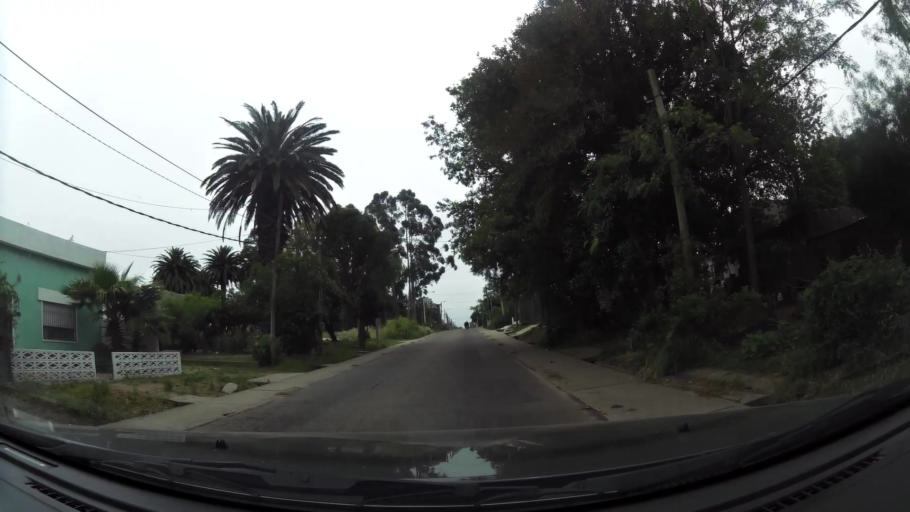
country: UY
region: Canelones
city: Las Piedras
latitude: -34.7309
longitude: -56.2277
